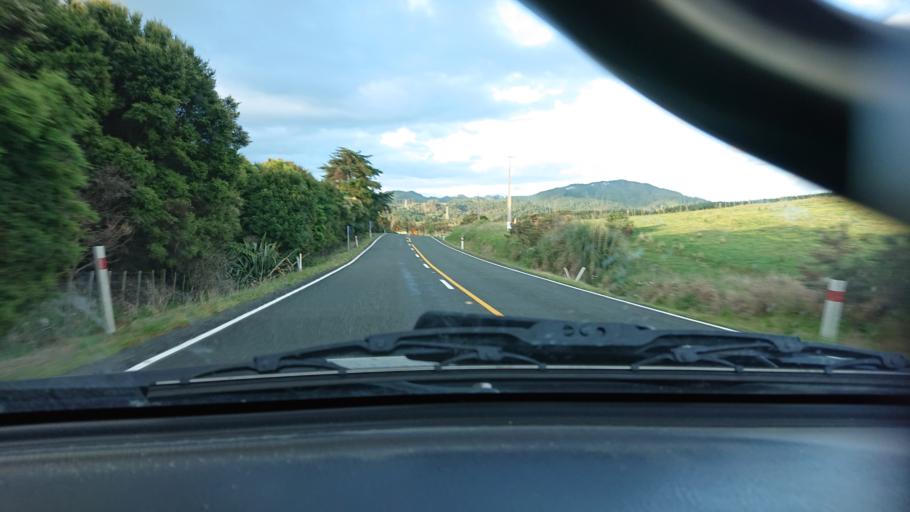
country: NZ
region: Auckland
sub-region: Auckland
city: Parakai
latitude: -36.5190
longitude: 174.4494
